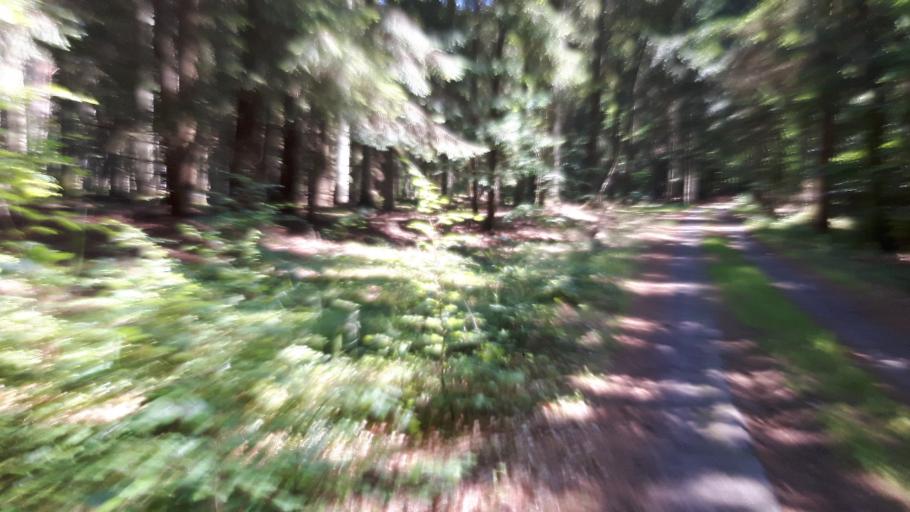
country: PL
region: Pomeranian Voivodeship
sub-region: Powiat slupski
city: Smoldzino
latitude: 54.6714
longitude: 17.1767
